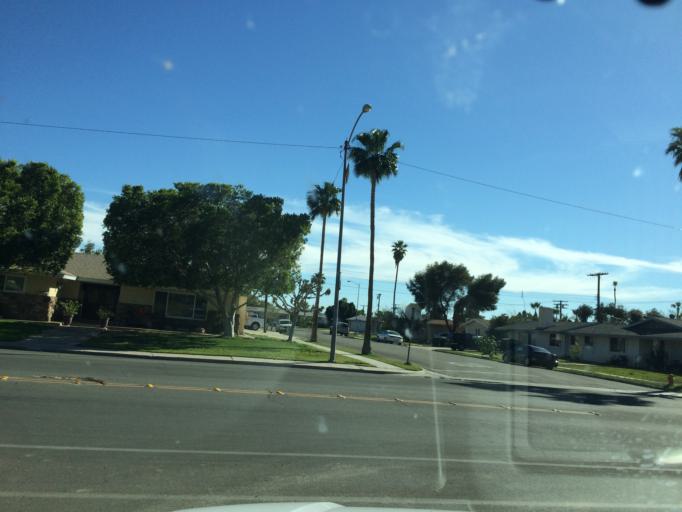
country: US
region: California
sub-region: Imperial County
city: El Centro
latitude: 32.7785
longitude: -115.5635
